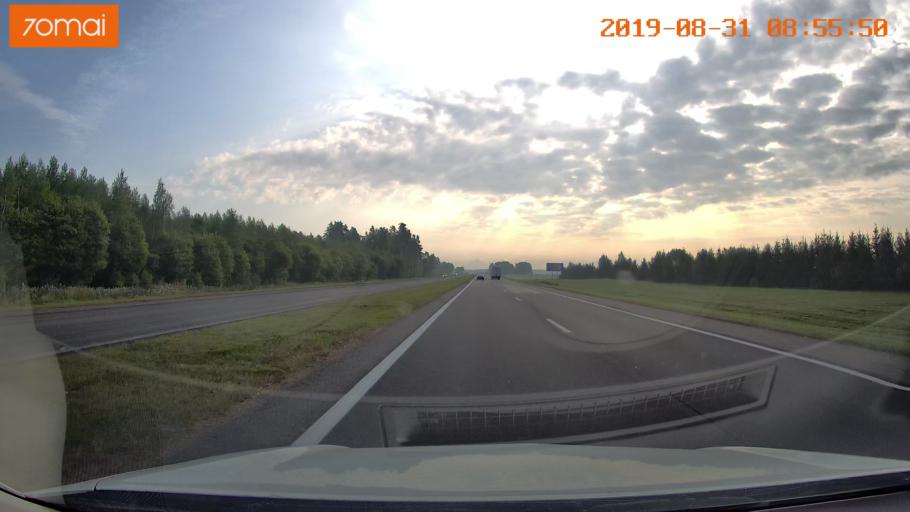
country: BY
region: Minsk
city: Smilavichy
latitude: 53.7643
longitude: 28.1168
